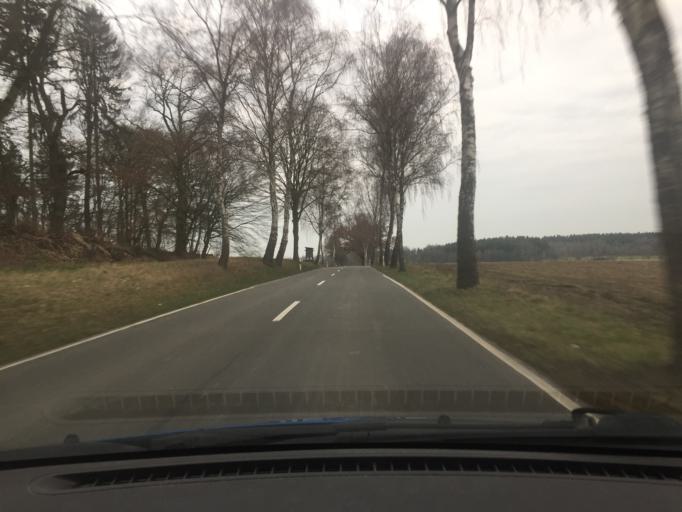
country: DE
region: Lower Saxony
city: Oetzen
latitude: 53.0324
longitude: 10.6698
